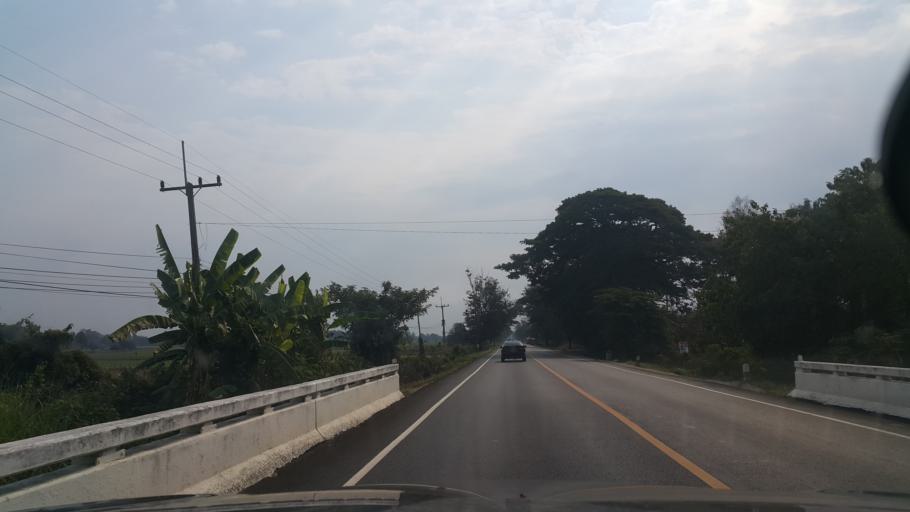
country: TH
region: Sukhothai
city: Si Samrong
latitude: 17.1794
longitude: 99.8413
